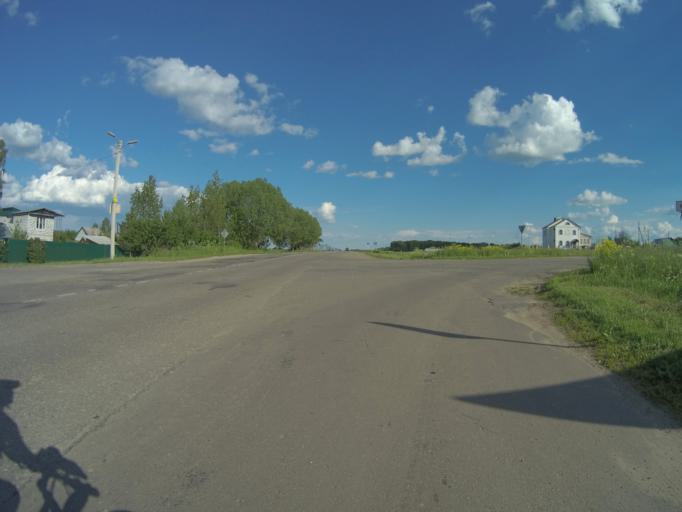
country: RU
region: Vladimir
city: Suzdal'
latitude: 56.4114
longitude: 40.4308
